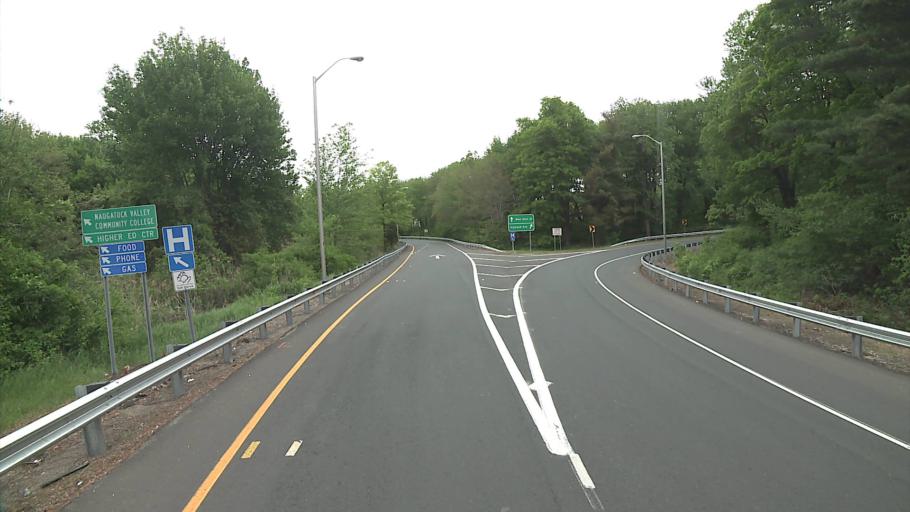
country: US
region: Connecticut
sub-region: New Haven County
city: Waterbury
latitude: 41.5496
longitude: -73.0630
